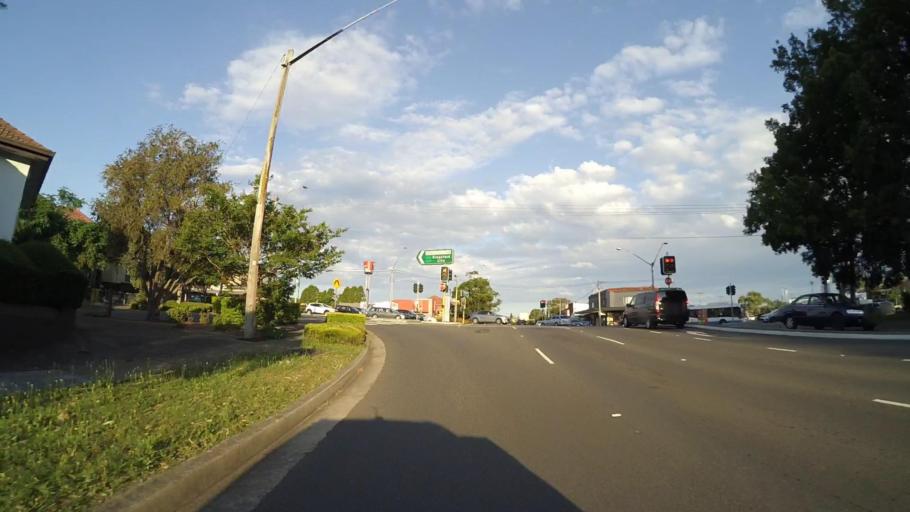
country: AU
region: New South Wales
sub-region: Randwick
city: Daceyville
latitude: -33.9400
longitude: 151.2280
